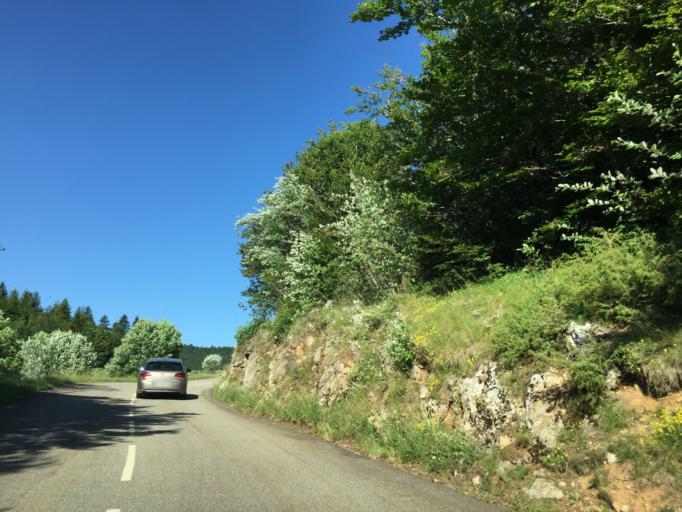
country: FR
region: Rhone-Alpes
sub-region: Departement de la Drome
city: Saint-Laurent-en-Royans
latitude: 44.9075
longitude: 5.3582
